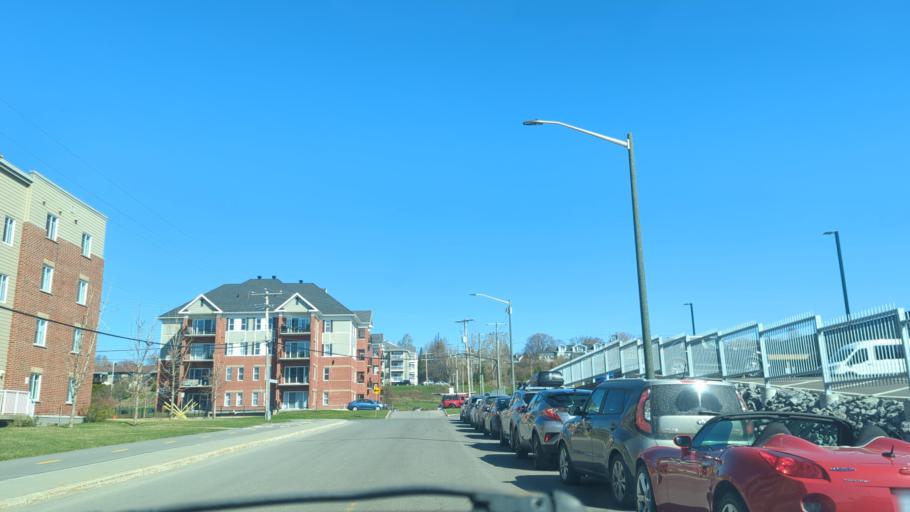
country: CA
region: Quebec
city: Quebec
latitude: 46.8470
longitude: -71.2636
